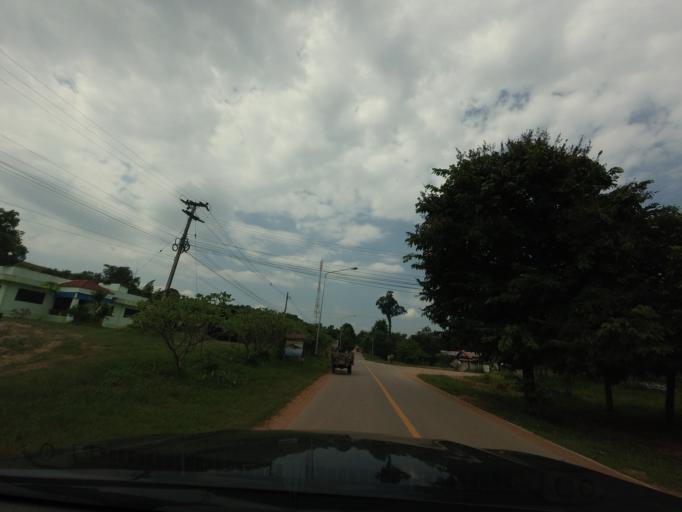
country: TH
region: Uttaradit
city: Fak Tha
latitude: 17.8025
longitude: 100.9339
